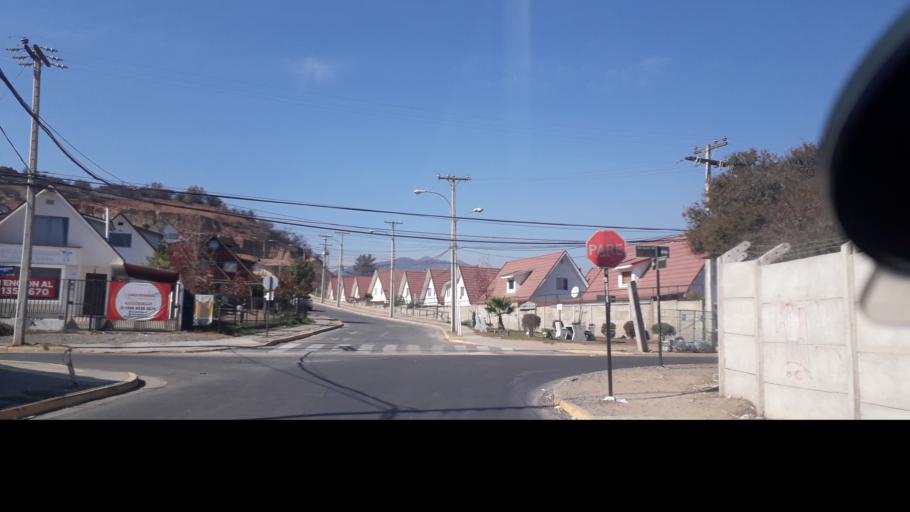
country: CL
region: Valparaiso
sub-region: Provincia de Marga Marga
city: Villa Alemana
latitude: -33.0491
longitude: -71.3442
